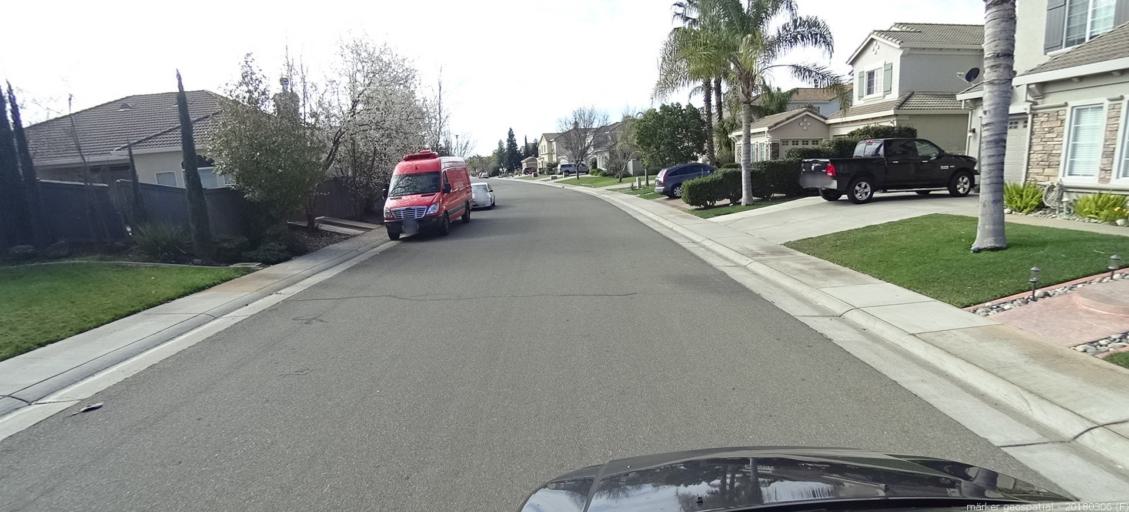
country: US
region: California
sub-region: Sacramento County
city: Vineyard
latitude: 38.4738
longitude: -121.3104
